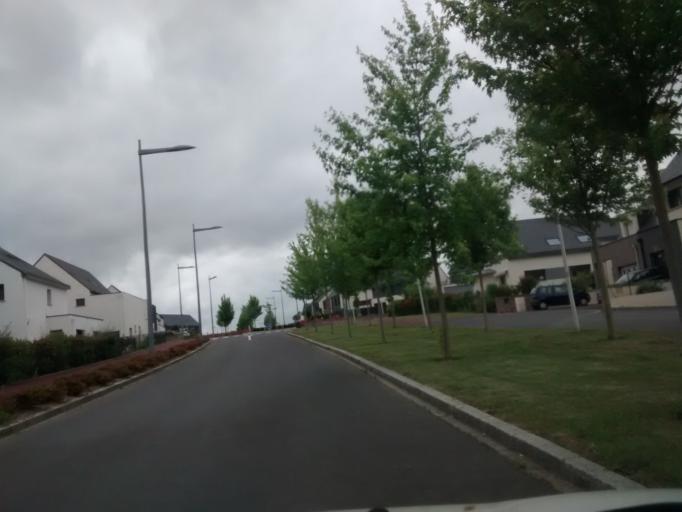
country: FR
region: Brittany
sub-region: Departement d'Ille-et-Vilaine
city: Saint-Gregoire
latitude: 48.1591
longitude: -1.6709
